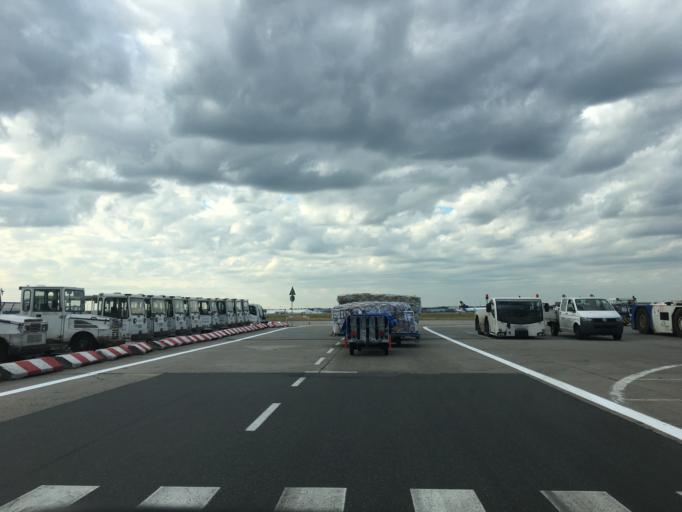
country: DE
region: Hesse
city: Kelsterbach
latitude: 50.0429
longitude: 8.5649
